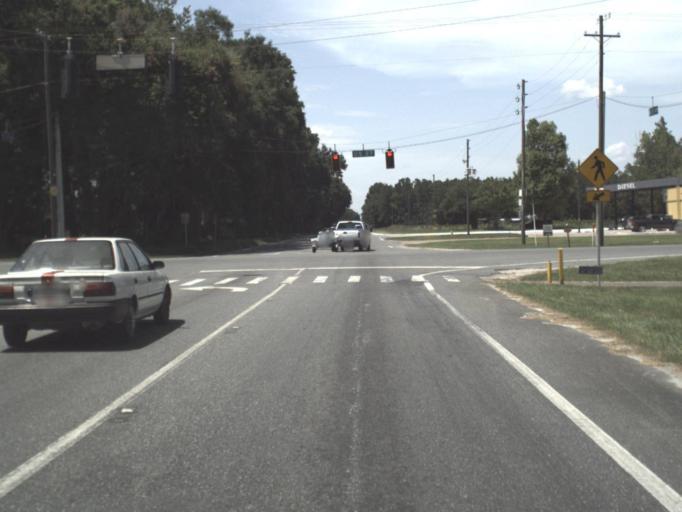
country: US
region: Florida
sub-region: Suwannee County
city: Wellborn
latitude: 29.9520
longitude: -82.8605
